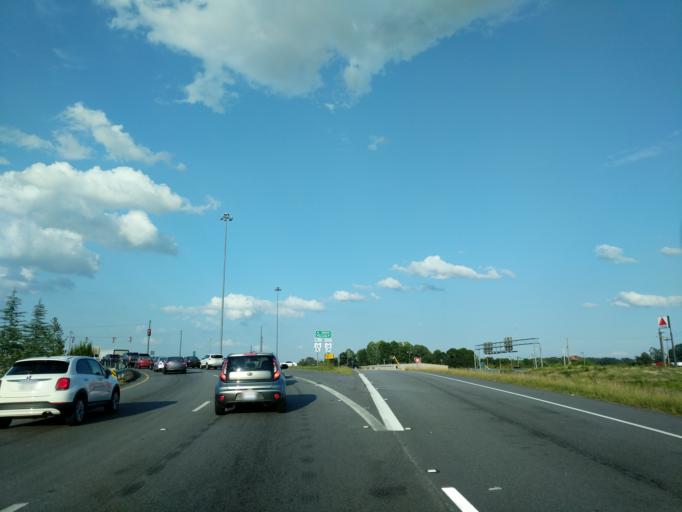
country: US
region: South Carolina
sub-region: Greenville County
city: Five Forks
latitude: 34.8711
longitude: -82.2256
